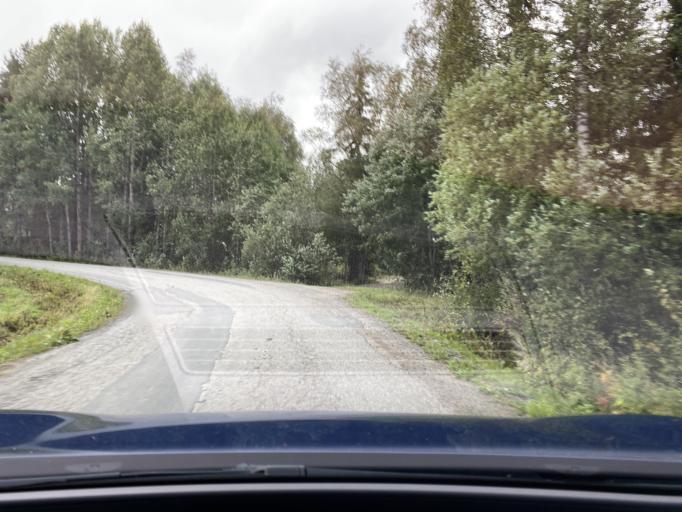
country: FI
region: Pirkanmaa
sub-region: Lounais-Pirkanmaa
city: Punkalaidun
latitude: 61.1690
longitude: 23.1781
